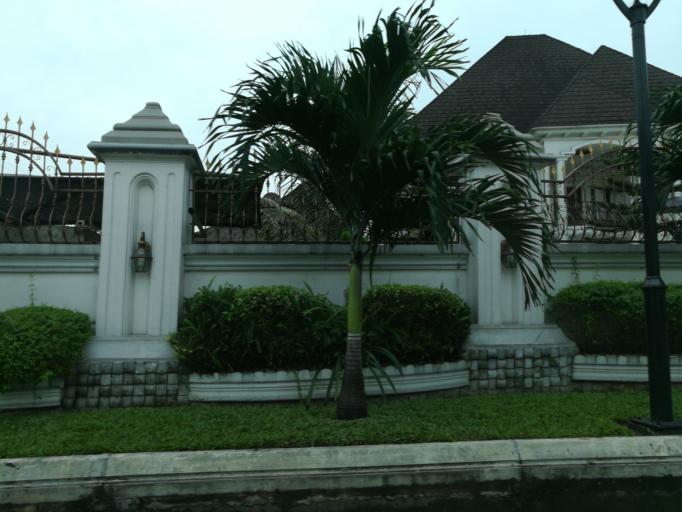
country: NG
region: Rivers
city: Port Harcourt
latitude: 4.8420
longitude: 7.0328
